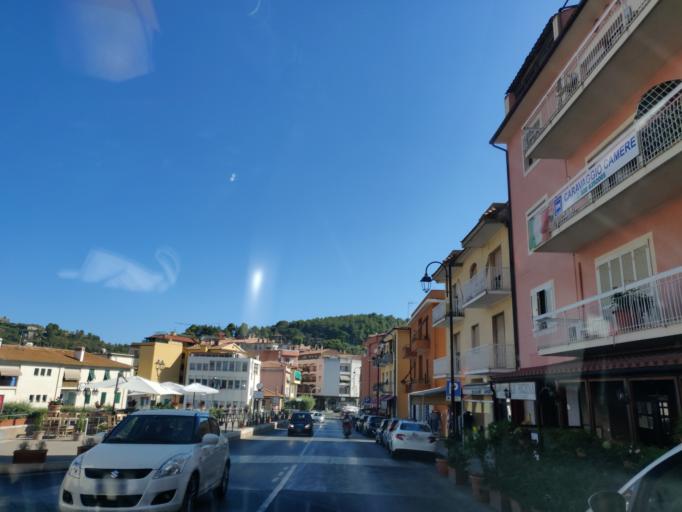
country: IT
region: Tuscany
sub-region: Provincia di Grosseto
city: Porto Ercole
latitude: 42.3949
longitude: 11.2036
